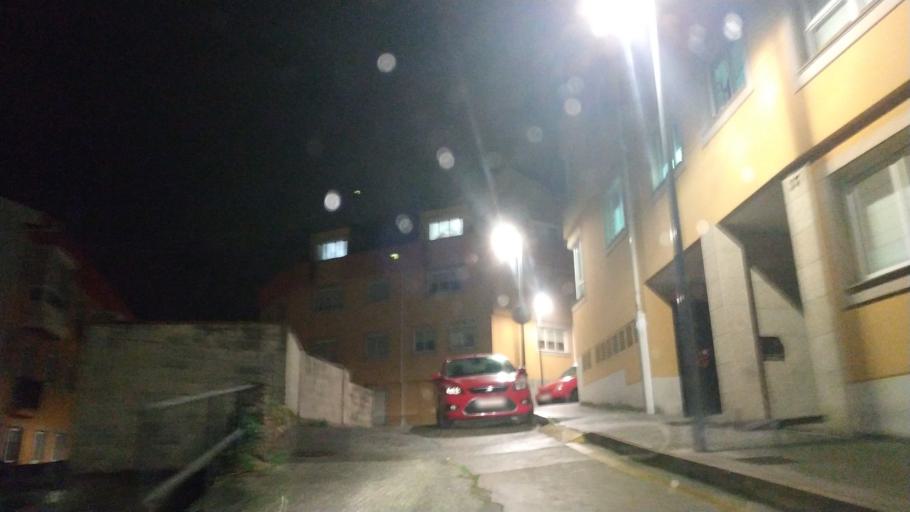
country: ES
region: Galicia
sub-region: Provincia da Coruna
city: Culleredo
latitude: 43.3277
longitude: -8.3915
